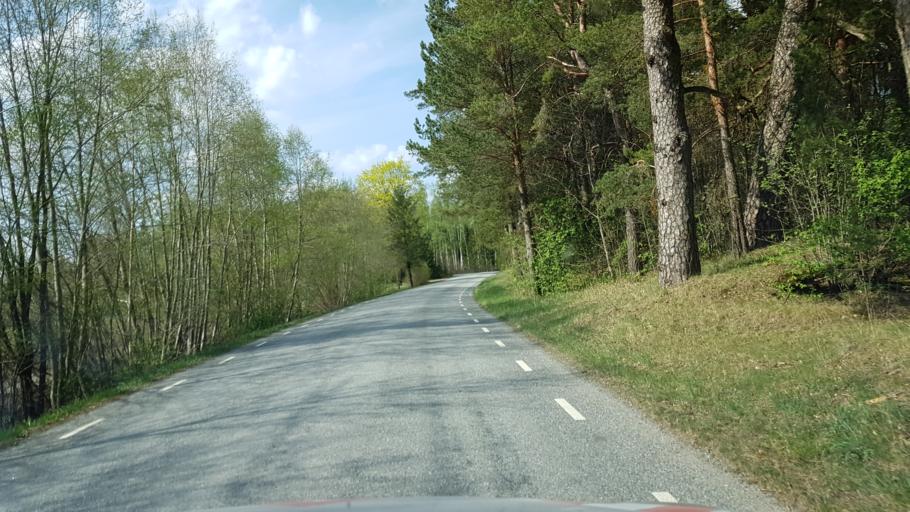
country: EE
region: Paernumaa
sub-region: Paikuse vald
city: Paikuse
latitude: 58.4395
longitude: 24.6089
